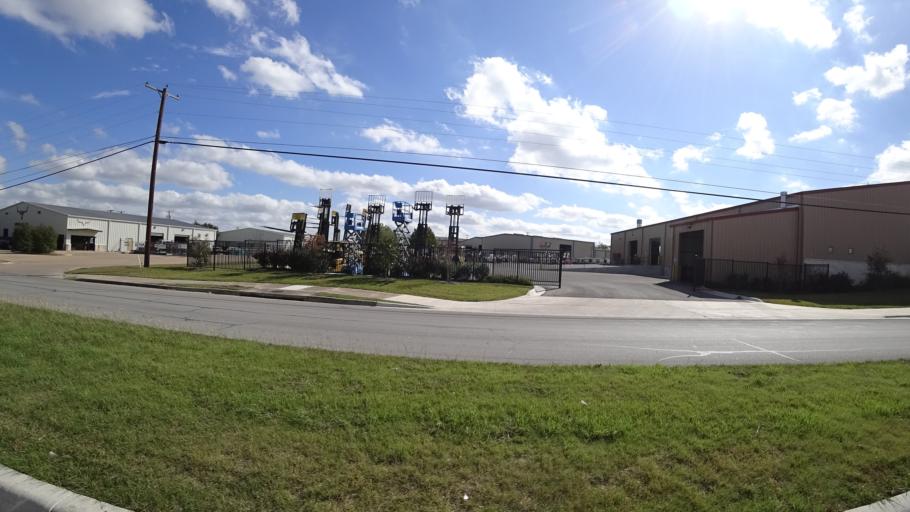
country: US
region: Texas
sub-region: Travis County
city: Windemere
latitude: 30.4670
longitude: -97.6603
